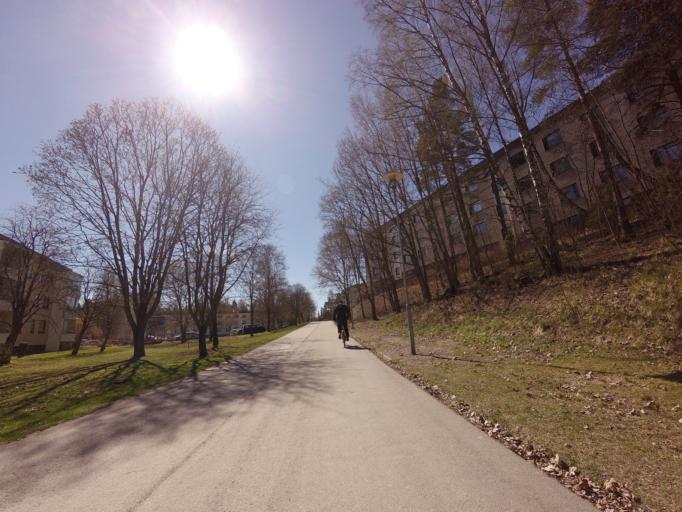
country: FI
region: Uusimaa
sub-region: Helsinki
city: Koukkuniemi
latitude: 60.1563
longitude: 24.7486
